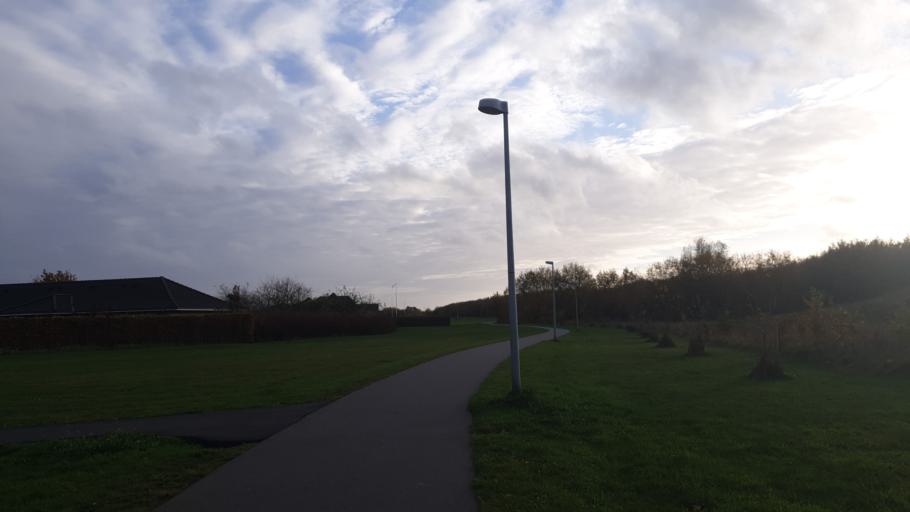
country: DK
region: Central Jutland
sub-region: Hedensted Kommune
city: Hedensted
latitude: 55.7892
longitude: 9.6927
